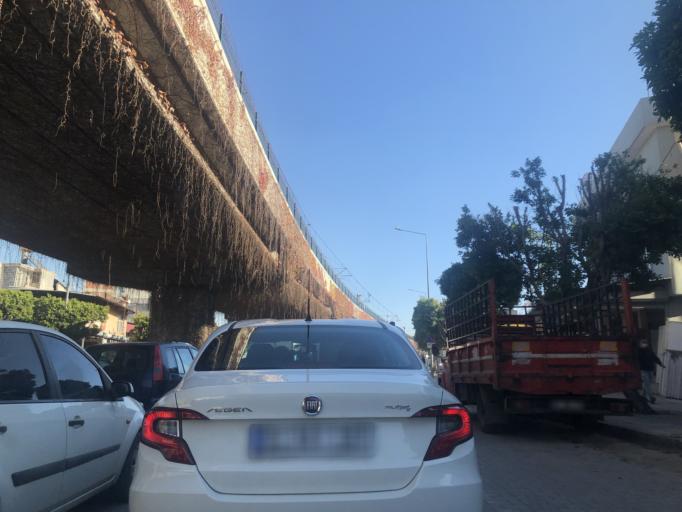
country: TR
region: Adana
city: Adana
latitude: 36.9800
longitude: 35.3309
